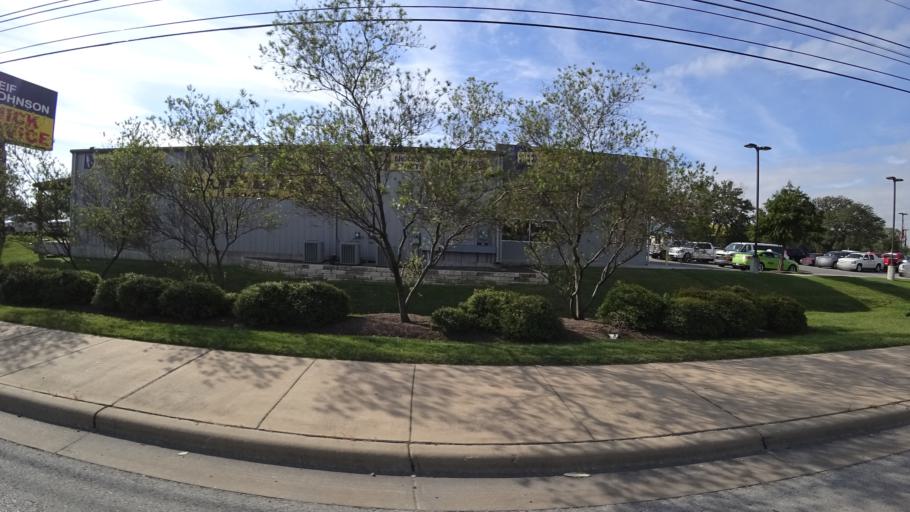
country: US
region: Texas
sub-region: Travis County
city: Austin
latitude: 30.2133
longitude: -97.7243
